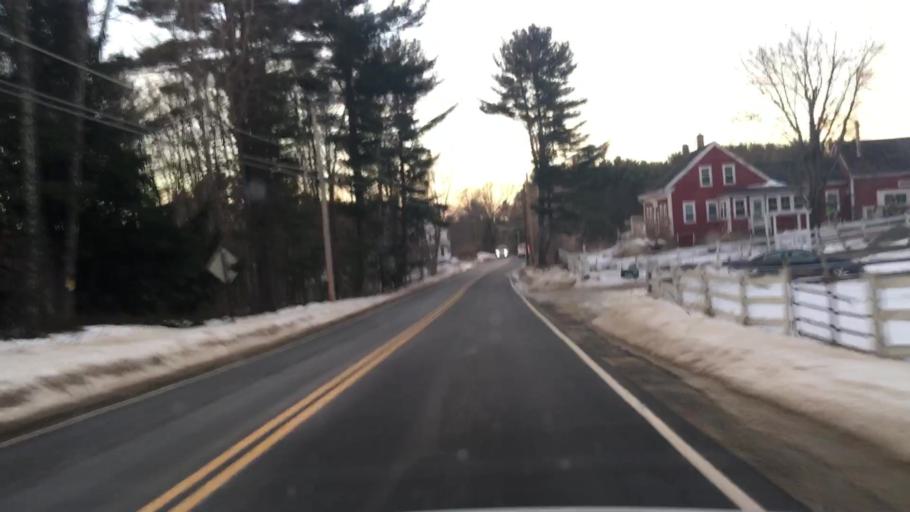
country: US
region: Maine
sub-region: York County
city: Lebanon
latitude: 43.4297
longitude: -70.8816
